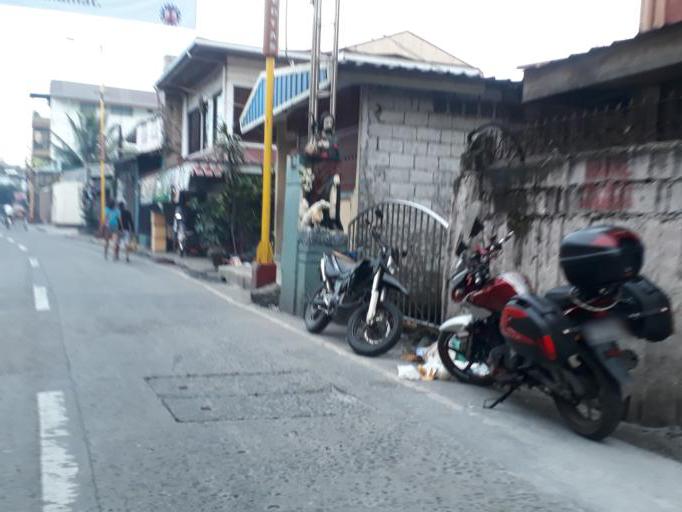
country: PH
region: Calabarzon
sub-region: Province of Rizal
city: Malabon
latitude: 14.6699
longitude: 120.9417
